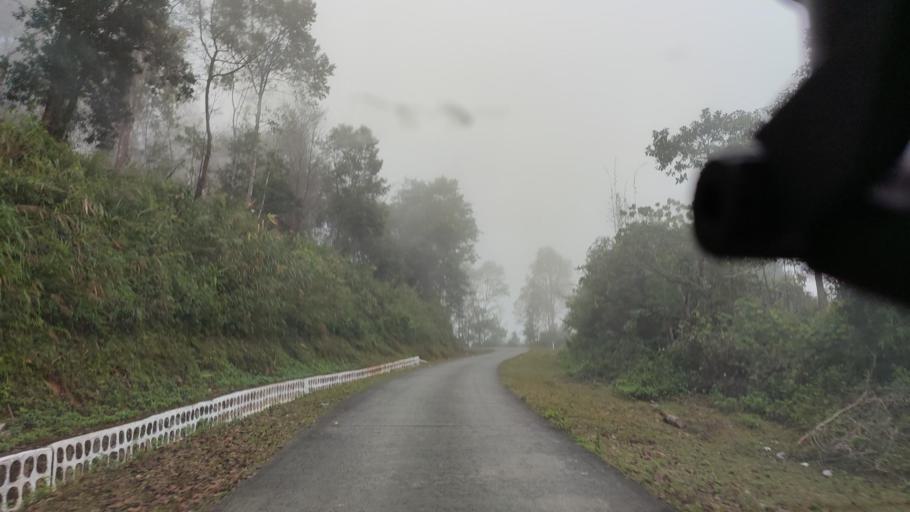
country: TH
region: Chiang Rai
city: Mae Sai
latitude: 21.1115
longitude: 99.6115
